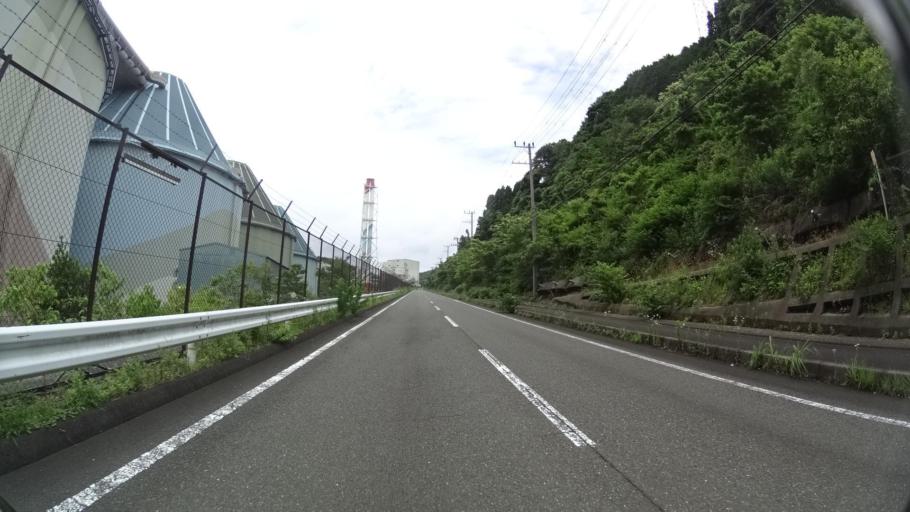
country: JP
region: Kyoto
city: Maizuru
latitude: 35.5255
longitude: 135.3457
